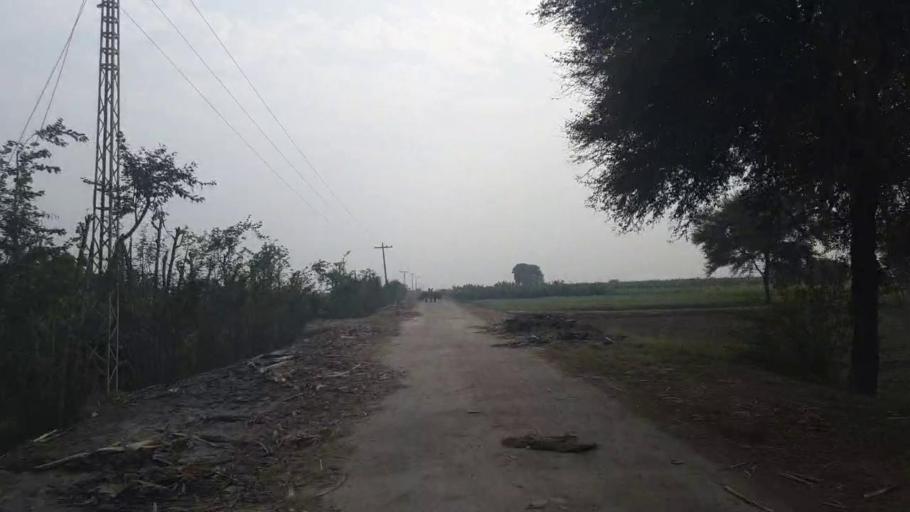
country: PK
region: Sindh
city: Berani
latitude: 25.7961
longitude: 68.7311
